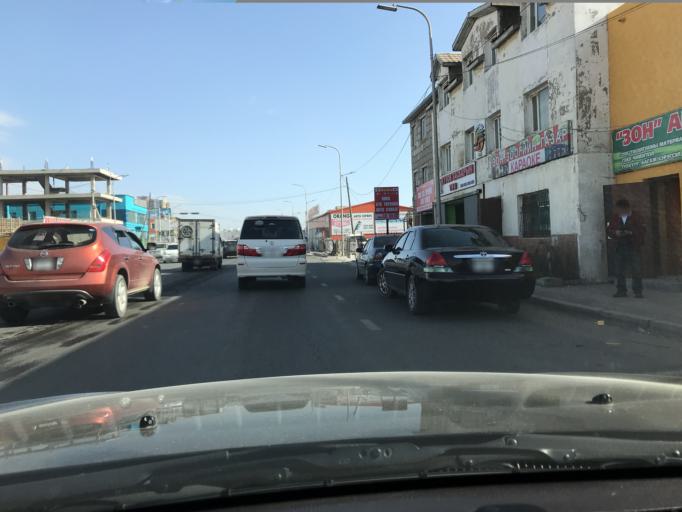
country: MN
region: Ulaanbaatar
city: Ulaanbaatar
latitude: 47.9235
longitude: 106.9596
